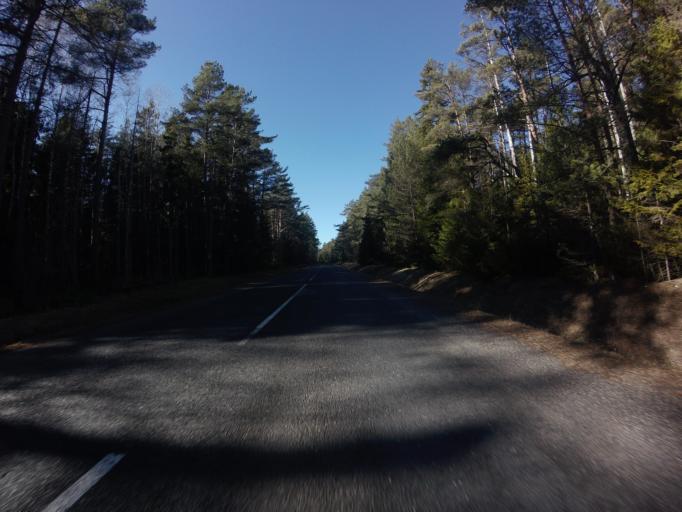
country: EE
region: Saare
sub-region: Kuressaare linn
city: Kuressaare
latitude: 58.5939
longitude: 22.6019
